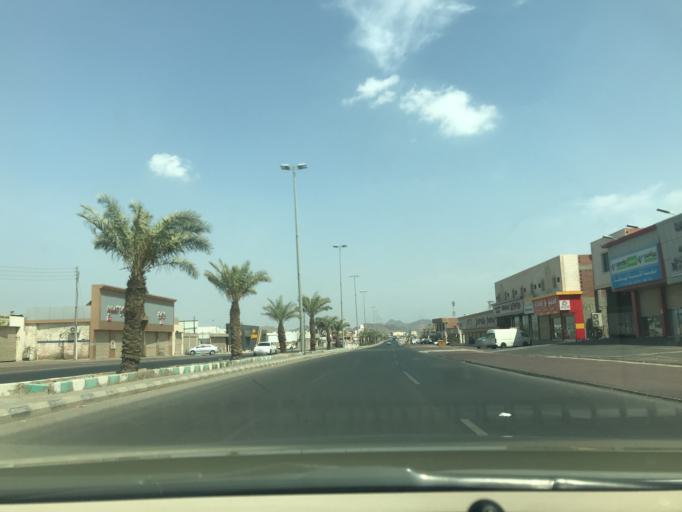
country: SA
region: Makkah
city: Al Jumum
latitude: 21.6230
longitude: 39.6825
